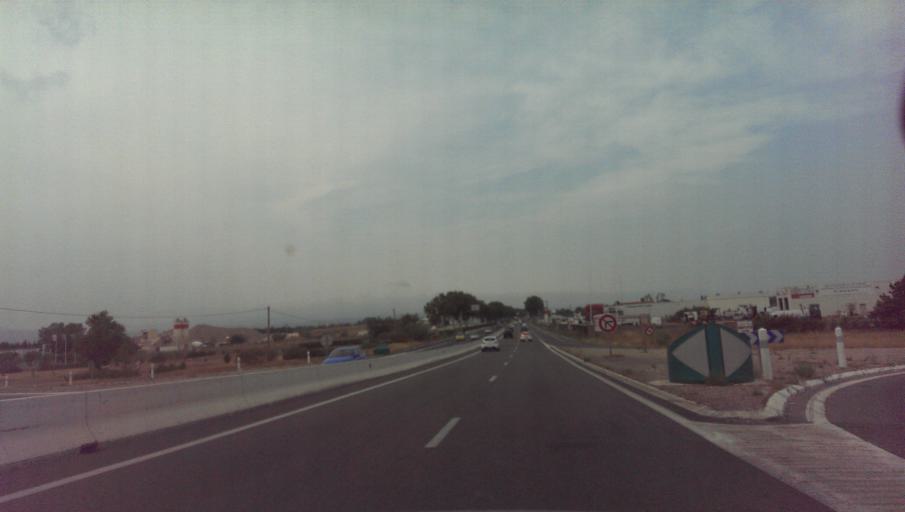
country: FR
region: Languedoc-Roussillon
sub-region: Departement des Pyrenees-Orientales
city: Pia
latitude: 42.7540
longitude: 2.8959
